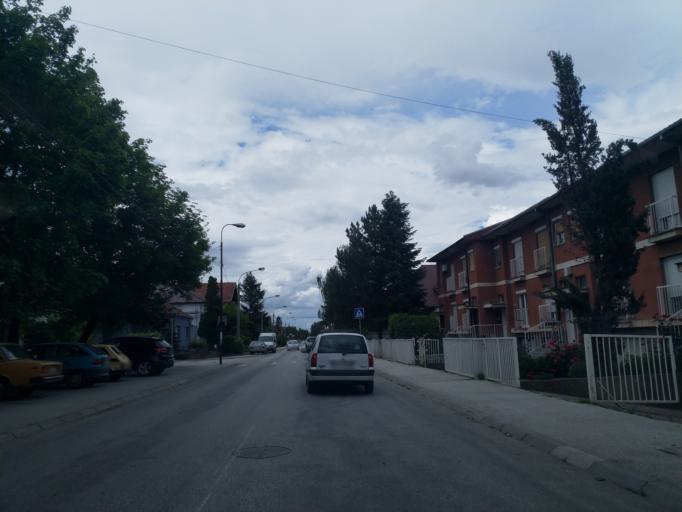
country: RS
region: Central Serbia
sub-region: Pomoravski Okrug
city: Jagodina
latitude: 43.9702
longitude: 21.2749
